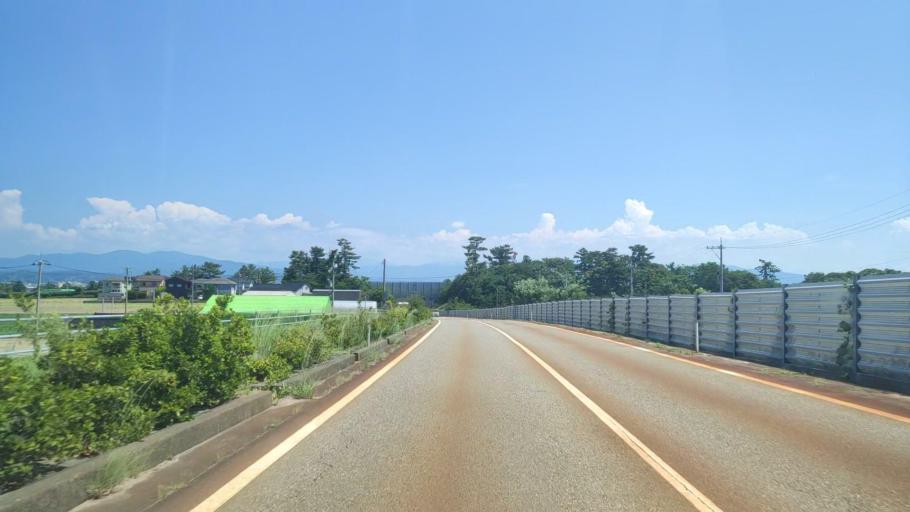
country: JP
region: Ishikawa
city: Kanazawa-shi
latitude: 36.6203
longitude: 136.6188
